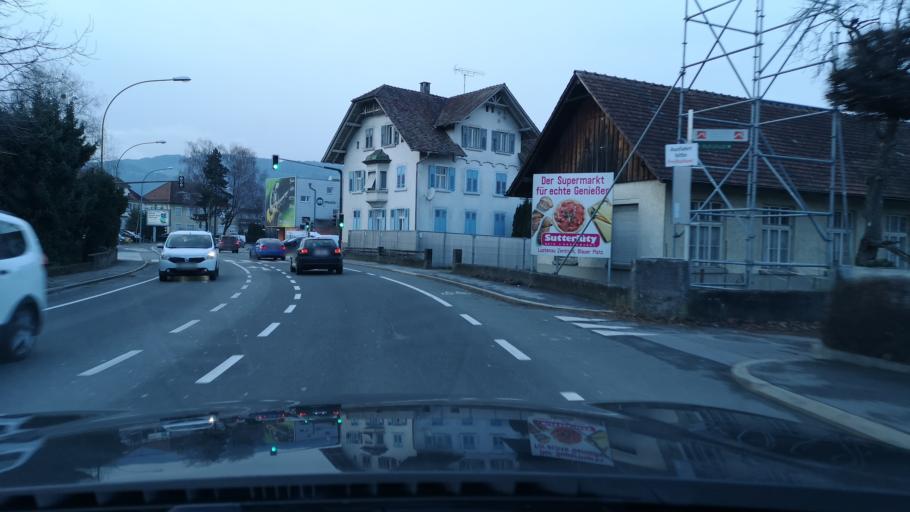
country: AT
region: Vorarlberg
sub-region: Politischer Bezirk Dornbirn
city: Lustenau
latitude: 47.4228
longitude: 9.6543
